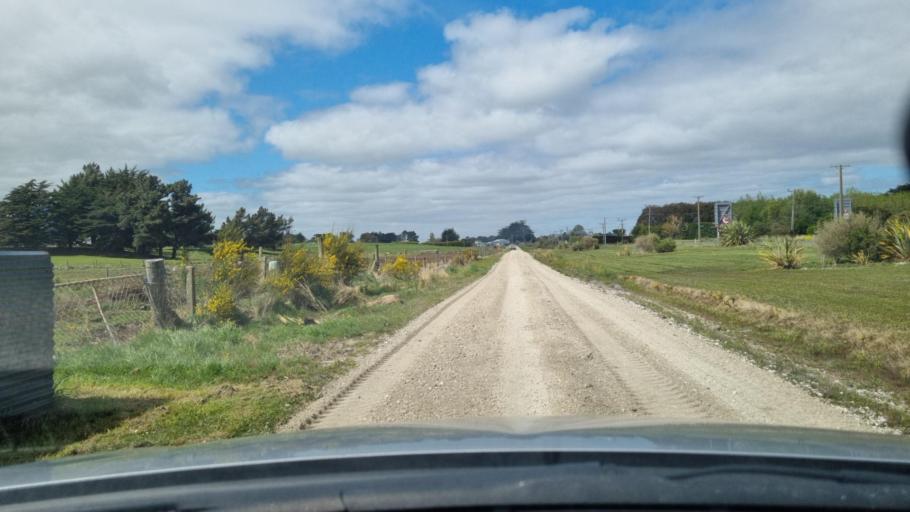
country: NZ
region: Southland
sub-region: Invercargill City
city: Invercargill
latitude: -46.4422
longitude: 168.3927
